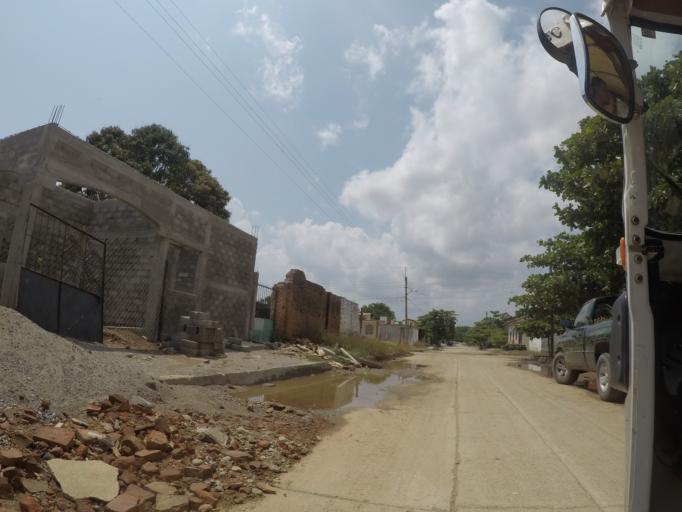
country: MX
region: Oaxaca
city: Union Hidalgo
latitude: 16.4774
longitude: -94.8269
